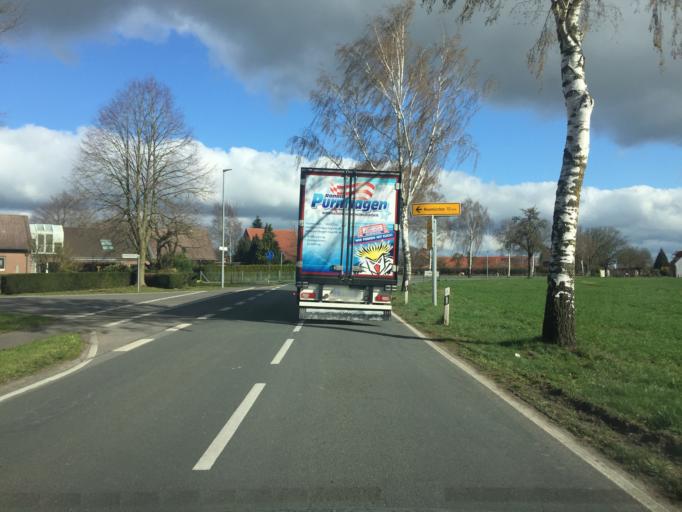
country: DE
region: Lower Saxony
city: Affinghausen
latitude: 52.7807
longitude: 8.8764
